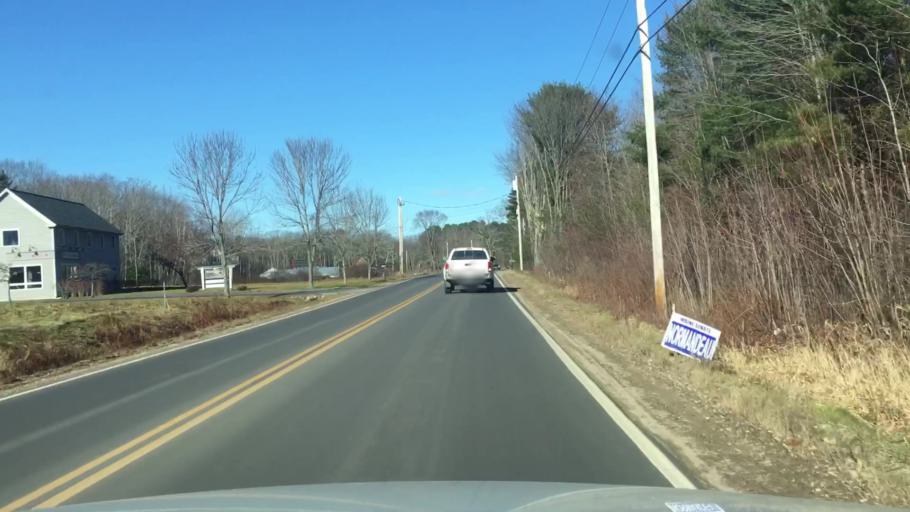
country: US
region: Maine
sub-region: York County
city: Arundel
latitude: 43.4092
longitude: -70.4937
